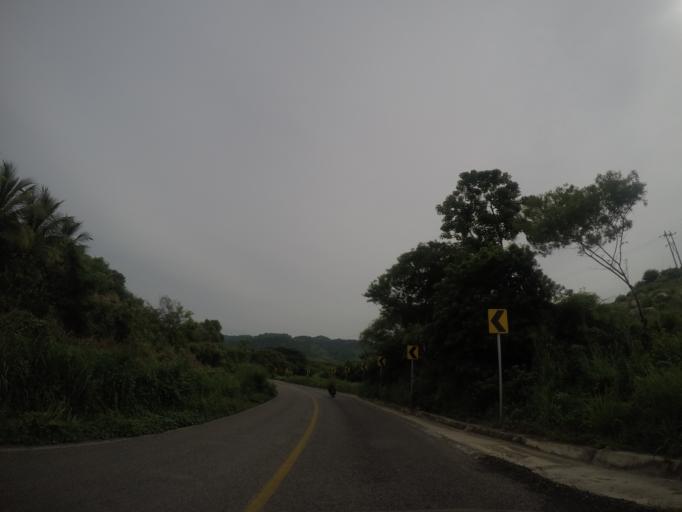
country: MX
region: Oaxaca
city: San Pedro Mixtepec
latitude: 15.9325
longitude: -97.1513
